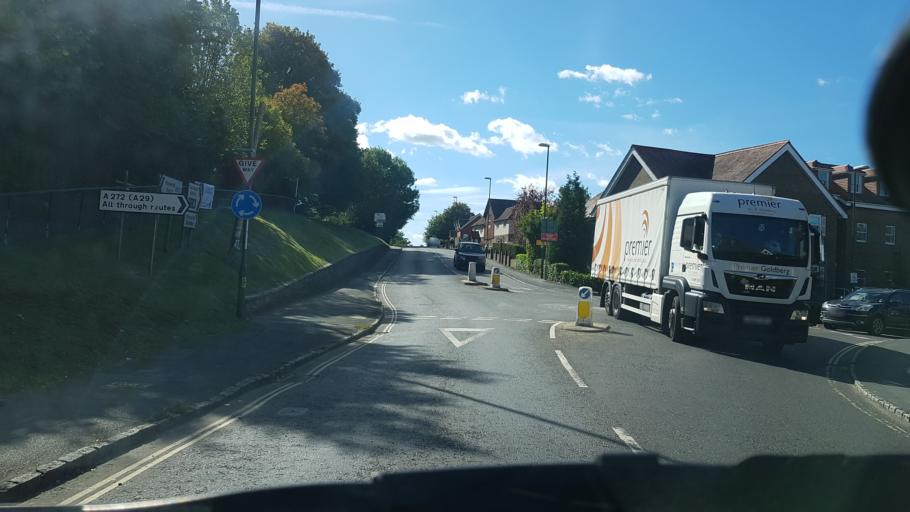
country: GB
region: England
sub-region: West Sussex
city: Billingshurst
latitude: 51.0209
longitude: -0.4526
